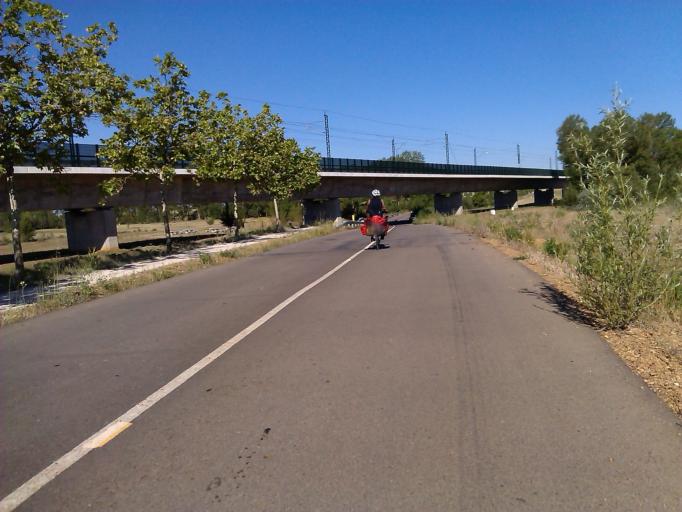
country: ES
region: Castille and Leon
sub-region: Provincia de Leon
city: Calzada del Coto
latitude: 42.3847
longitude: -5.1089
